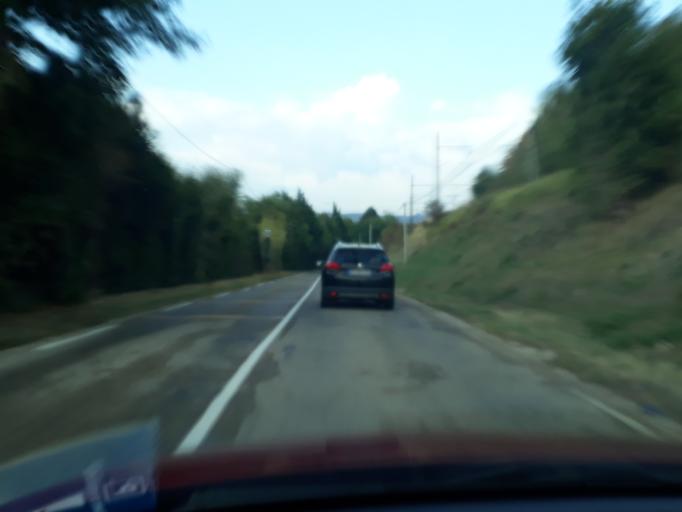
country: FR
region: Rhone-Alpes
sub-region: Departement du Rhone
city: Condrieu
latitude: 45.4702
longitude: 4.7913
